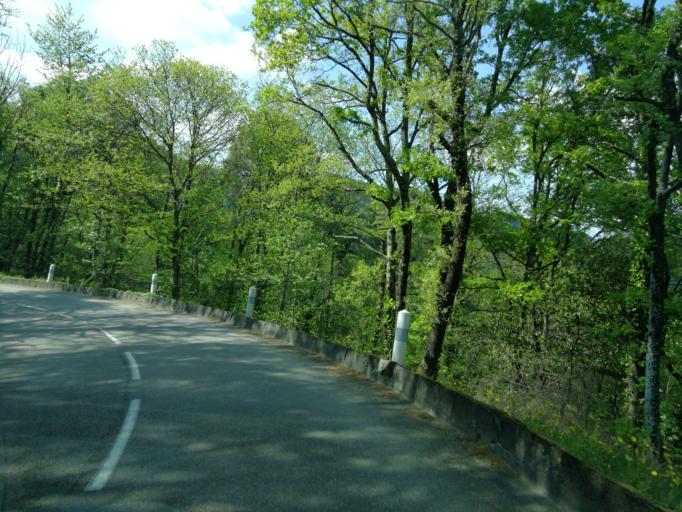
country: FR
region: Rhone-Alpes
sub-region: Departement de l'Ardeche
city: Saint-Sauveur-de-Montagut
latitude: 44.7997
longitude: 4.6131
